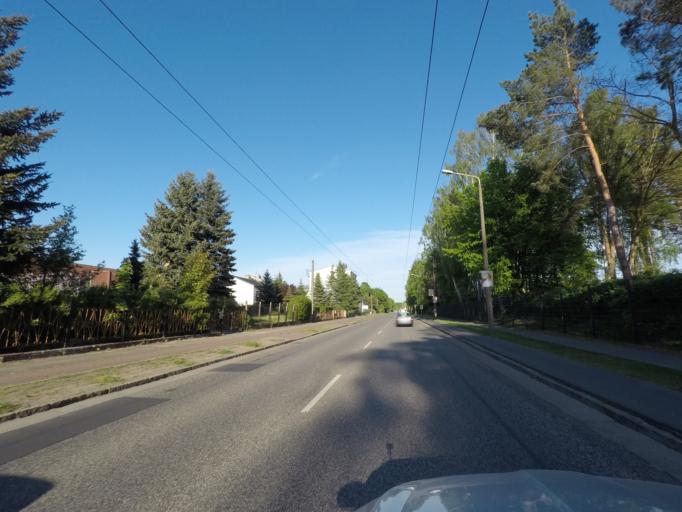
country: DE
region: Brandenburg
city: Melchow
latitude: 52.8382
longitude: 13.7416
